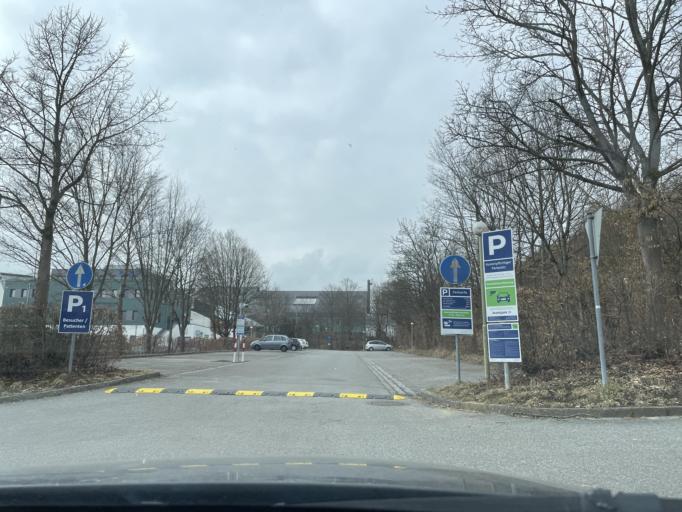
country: DE
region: Bavaria
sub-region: Lower Bavaria
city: Viechtach
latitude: 49.0862
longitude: 12.8773
